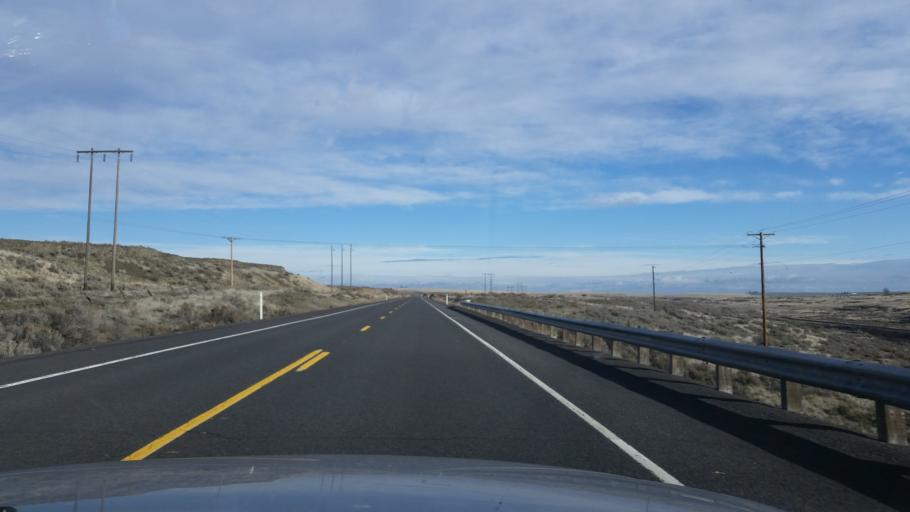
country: US
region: Washington
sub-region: Adams County
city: Ritzville
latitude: 47.3644
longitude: -118.4679
